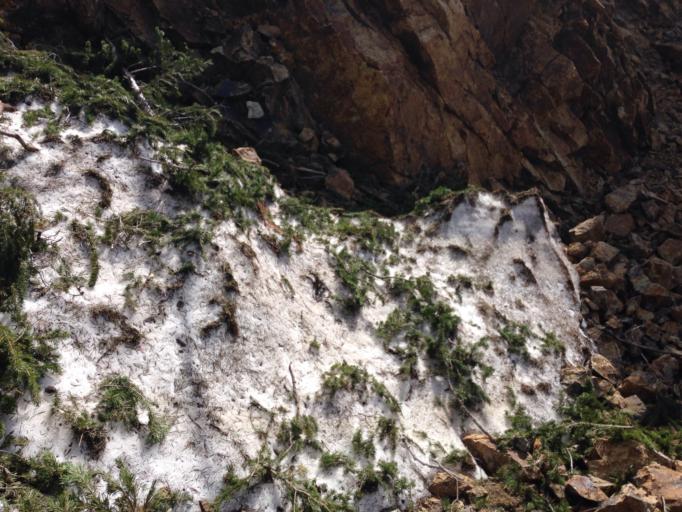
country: US
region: Colorado
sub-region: Larimer County
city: Estes Park
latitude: 40.4975
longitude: -105.8912
